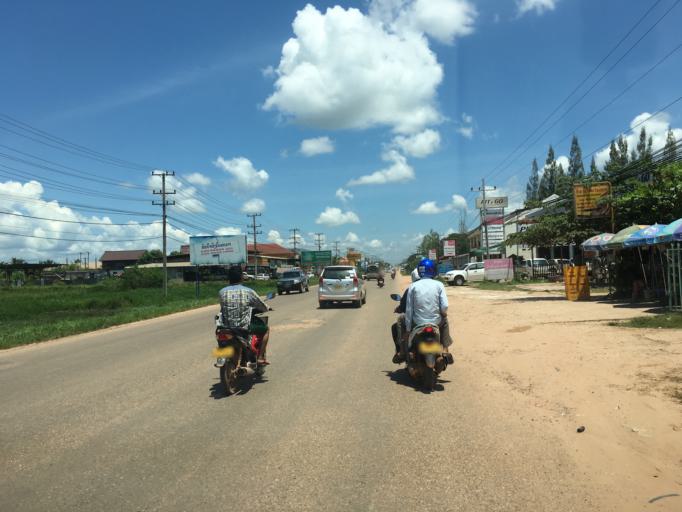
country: LA
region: Vientiane
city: Vientiane
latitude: 18.0347
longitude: 102.5477
